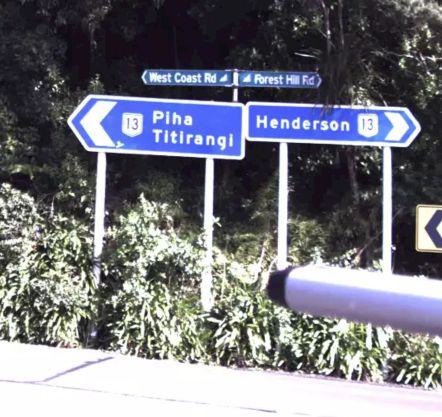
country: NZ
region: Auckland
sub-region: Auckland
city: Titirangi
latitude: -36.9305
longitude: 174.5814
